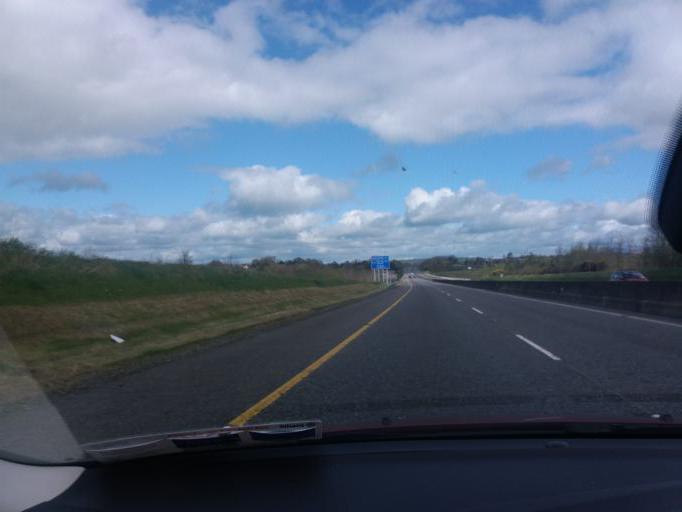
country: IE
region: Munster
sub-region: County Cork
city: Fermoy
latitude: 52.1362
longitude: -8.2606
